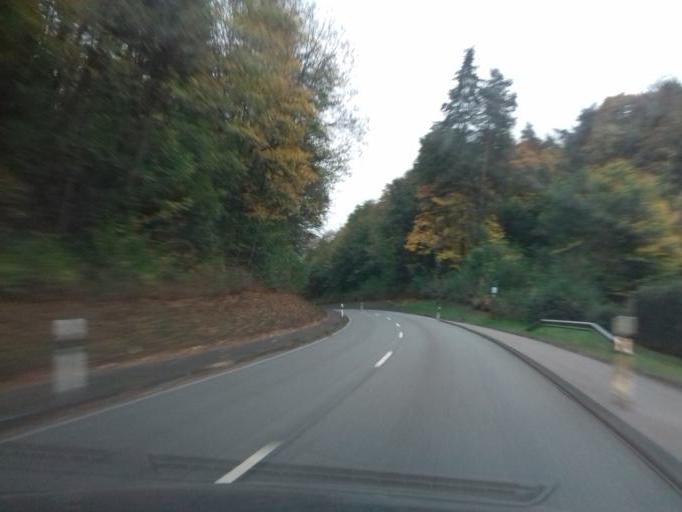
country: DE
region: Rheinland-Pfalz
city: Tawern
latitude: 49.6603
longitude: 6.5263
